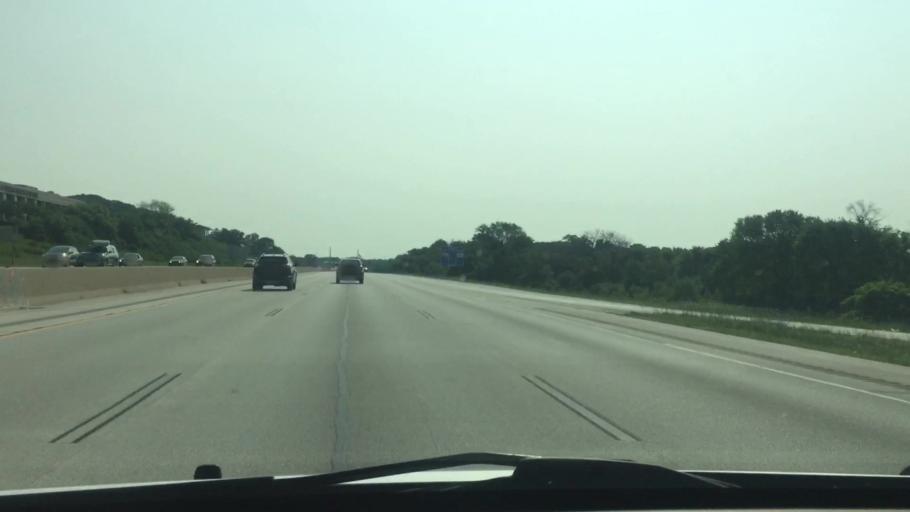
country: US
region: Wisconsin
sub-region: Waukesha County
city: Waukesha
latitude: 43.0488
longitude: -88.2230
